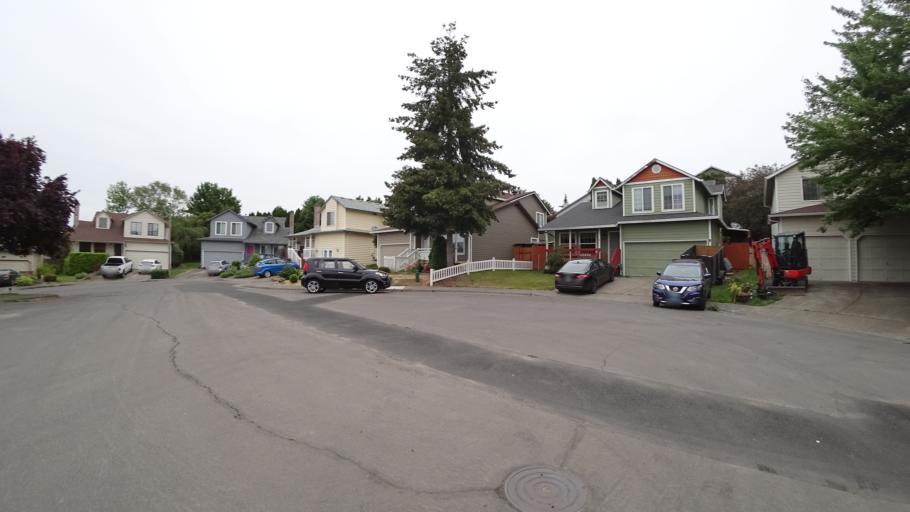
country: US
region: Oregon
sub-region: Washington County
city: Bethany
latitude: 45.5592
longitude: -122.8625
